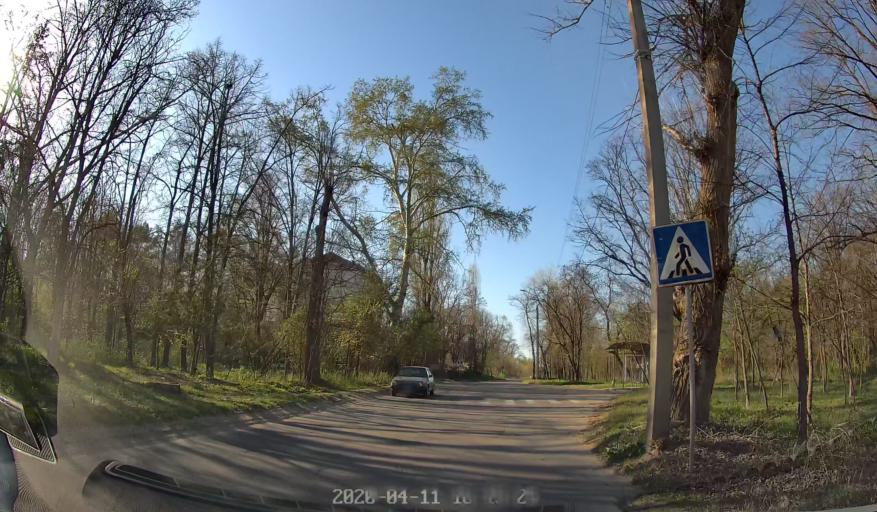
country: MD
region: Chisinau
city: Vadul lui Voda
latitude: 47.0795
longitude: 29.0933
